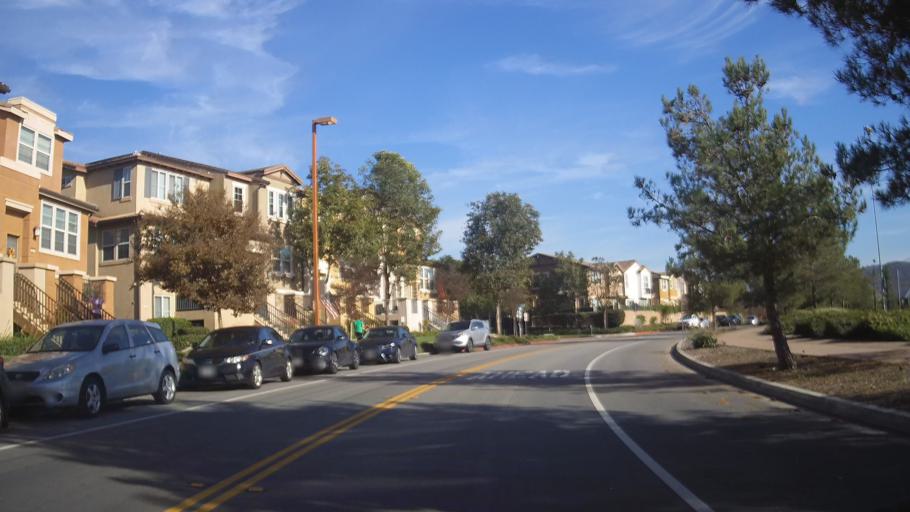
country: US
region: California
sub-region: San Diego County
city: Santee
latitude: 32.8524
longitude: -116.9805
